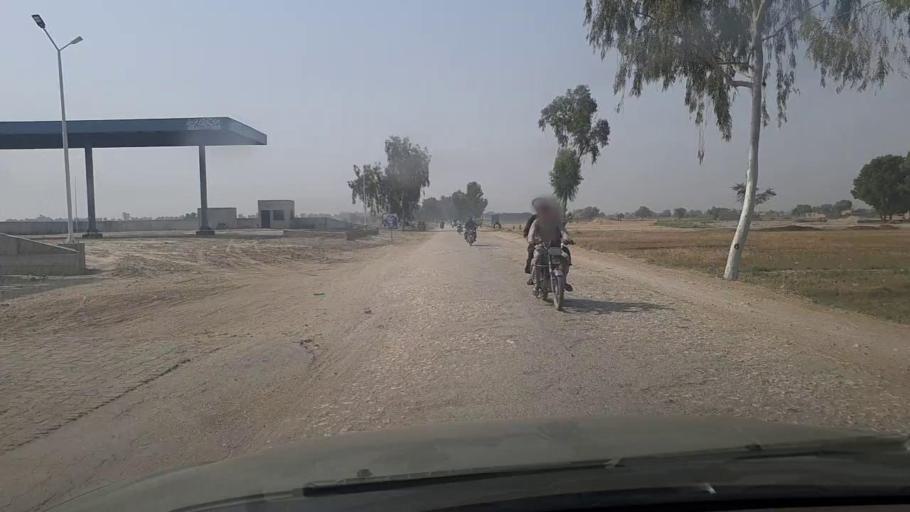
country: PK
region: Sindh
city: Mirpur Mathelo
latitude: 28.0074
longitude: 69.5472
